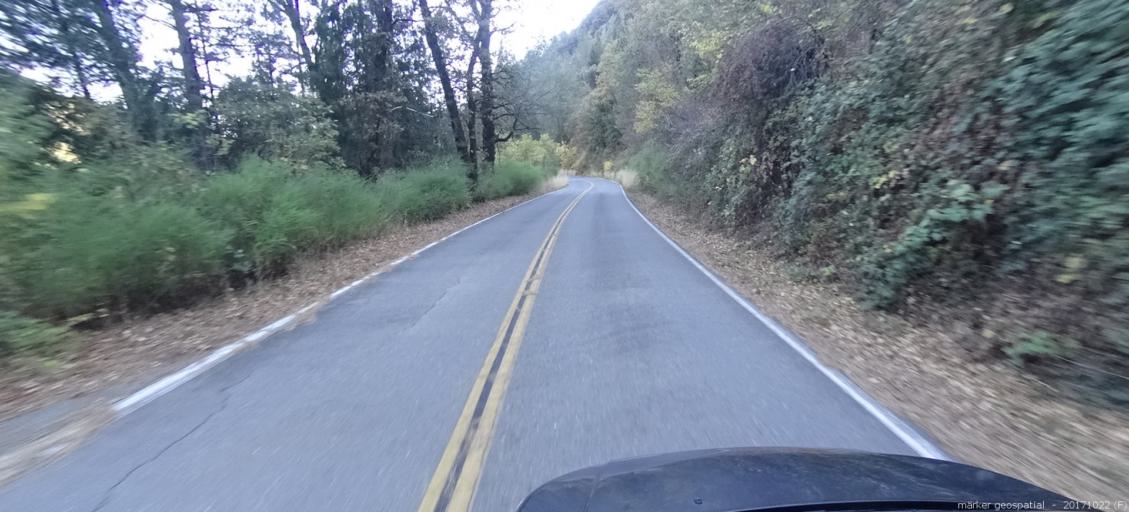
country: US
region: California
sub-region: Shasta County
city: Shasta Lake
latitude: 40.9264
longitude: -122.2487
